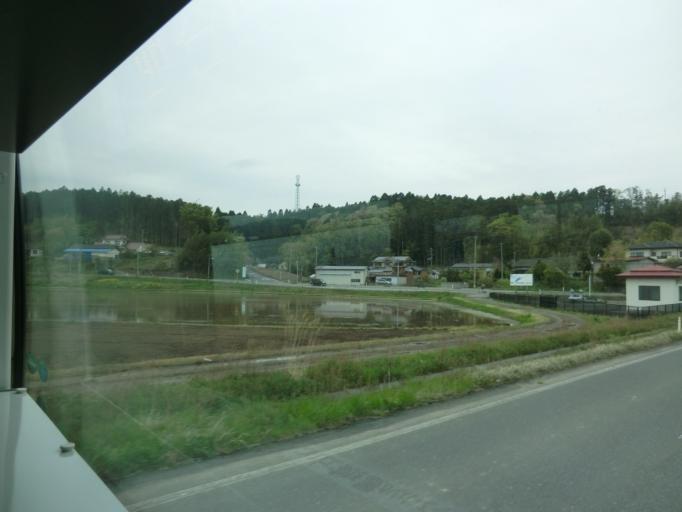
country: JP
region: Miyagi
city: Wakuya
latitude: 38.5642
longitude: 141.2680
